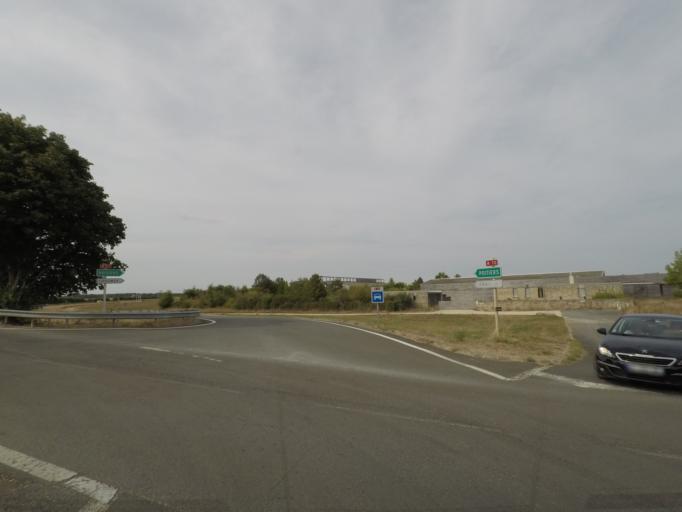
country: FR
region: Poitou-Charentes
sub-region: Departement de la Vienne
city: Chaunay
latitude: 46.1710
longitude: 0.1697
